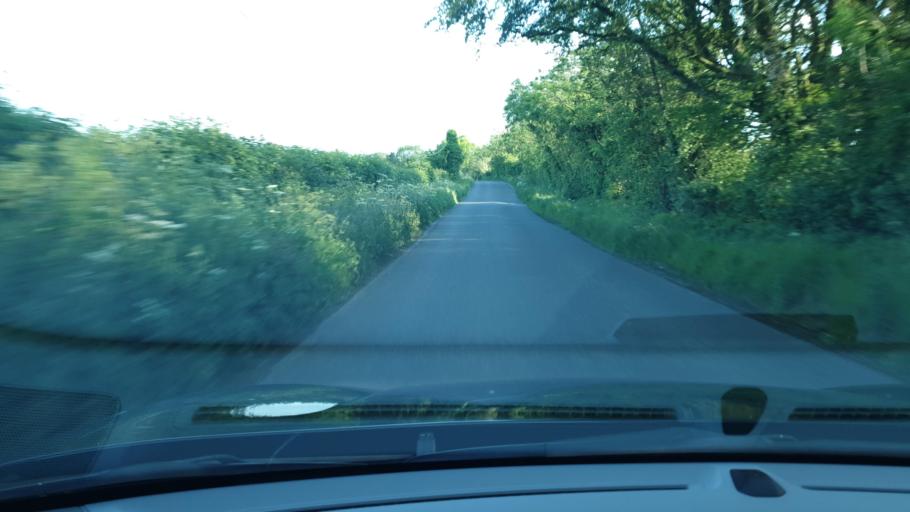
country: IE
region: Leinster
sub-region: An Mhi
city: Ashbourne
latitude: 53.5160
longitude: -6.3454
